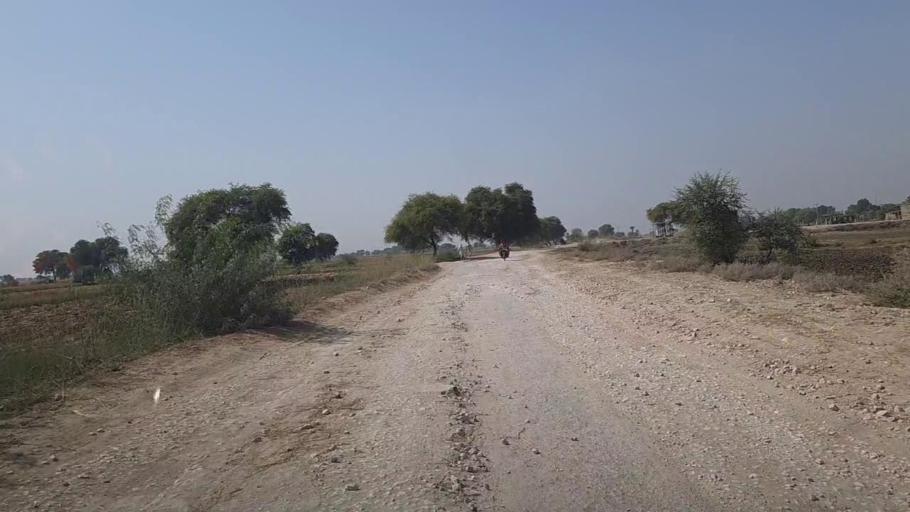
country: PK
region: Sindh
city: Kandhkot
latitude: 28.3884
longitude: 69.3289
